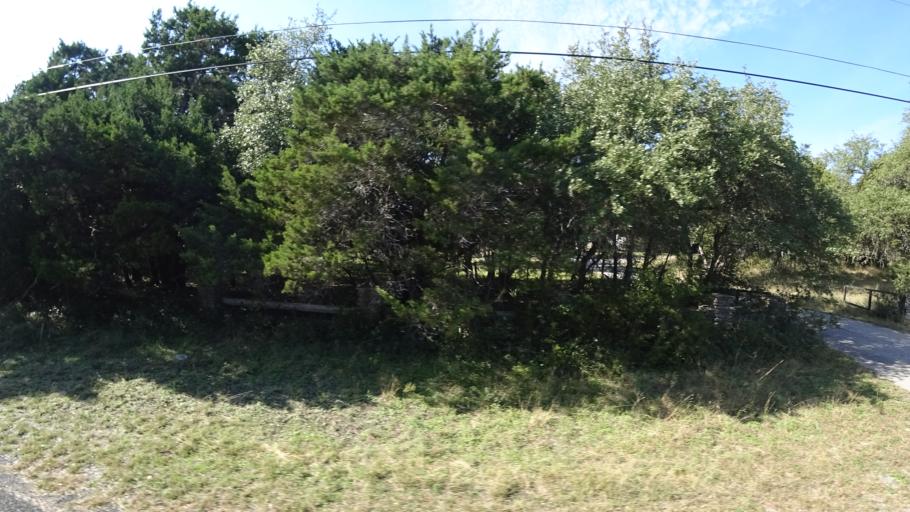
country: US
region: Texas
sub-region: Travis County
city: Barton Creek
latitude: 30.2267
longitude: -97.9159
